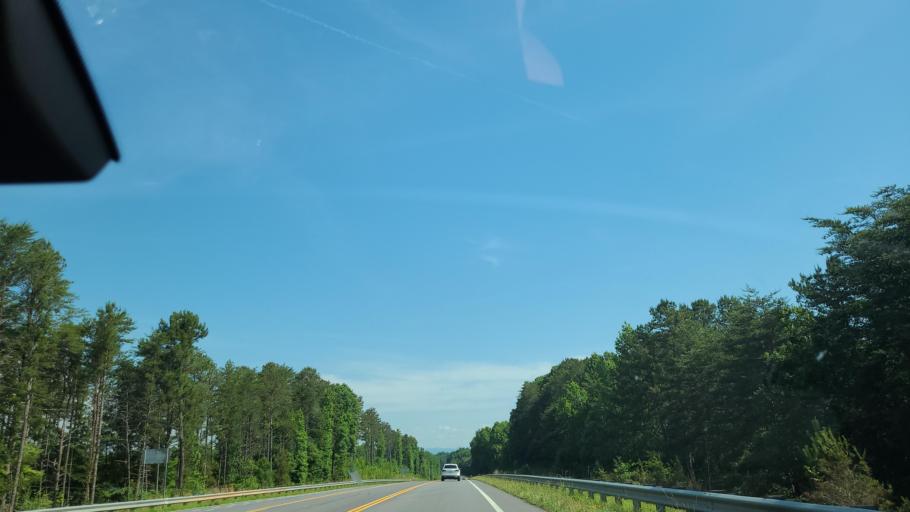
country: US
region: South Carolina
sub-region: Oconee County
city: Westminster
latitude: 34.7012
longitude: -83.0506
